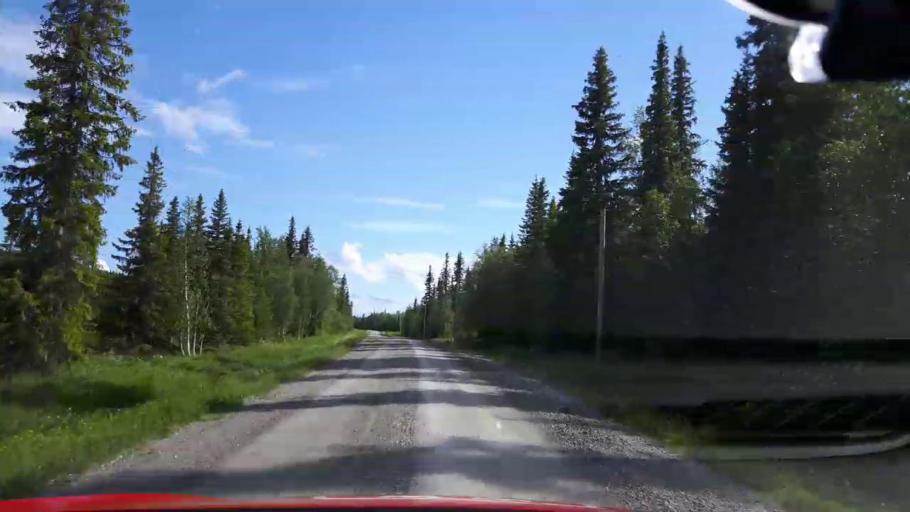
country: SE
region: Jaemtland
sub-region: Krokoms Kommun
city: Valla
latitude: 63.7923
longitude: 14.0465
